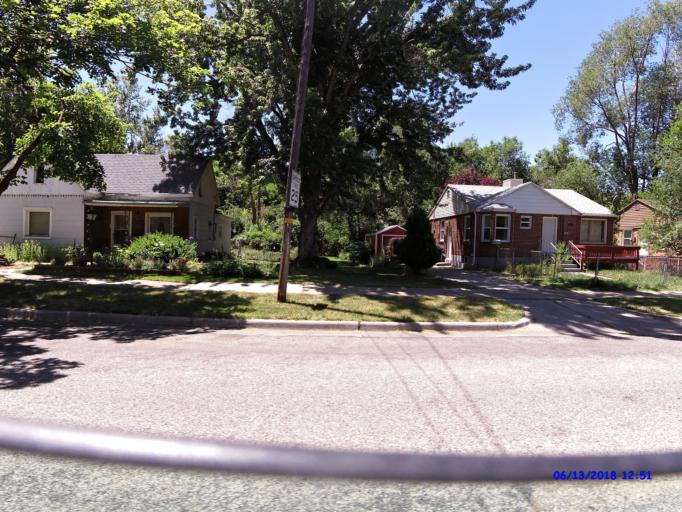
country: US
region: Utah
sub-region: Weber County
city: South Ogden
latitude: 41.2073
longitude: -111.9557
